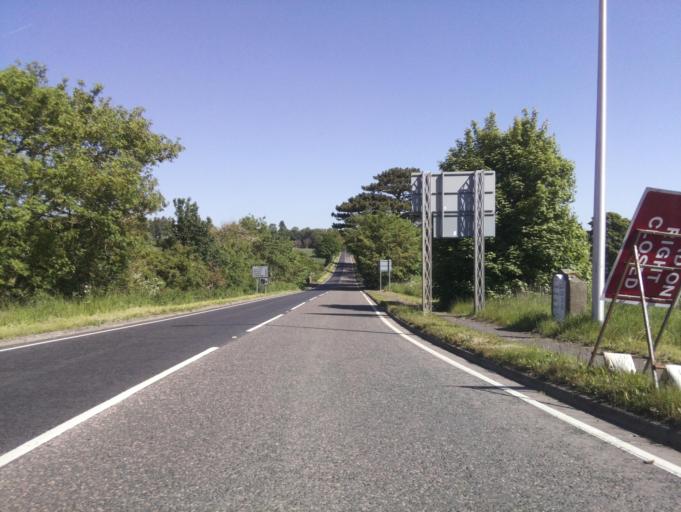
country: GB
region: Scotland
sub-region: Fife
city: Balmullo
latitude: 56.3490
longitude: -2.9416
